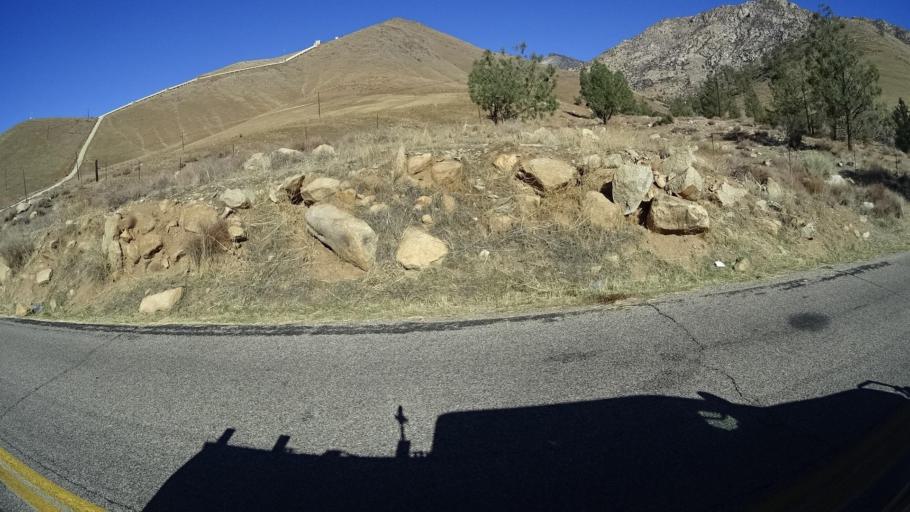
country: US
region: California
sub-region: Kern County
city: Kernville
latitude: 35.7744
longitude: -118.4321
